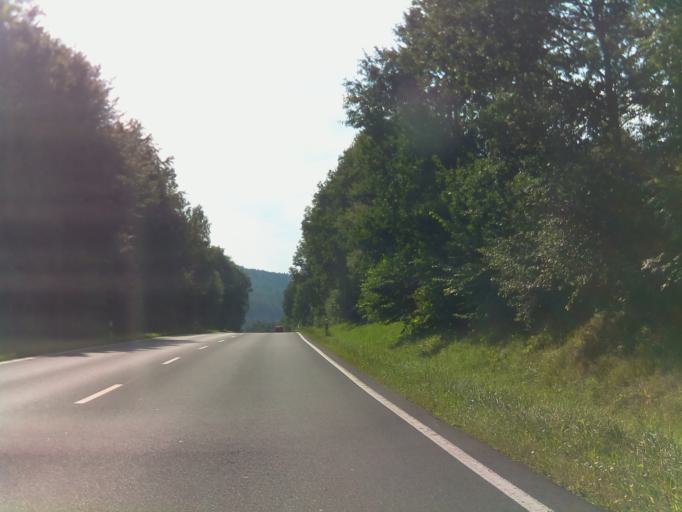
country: DE
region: Bavaria
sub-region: Regierungsbezirk Unterfranken
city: Riedenberg
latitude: 50.3168
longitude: 9.8605
